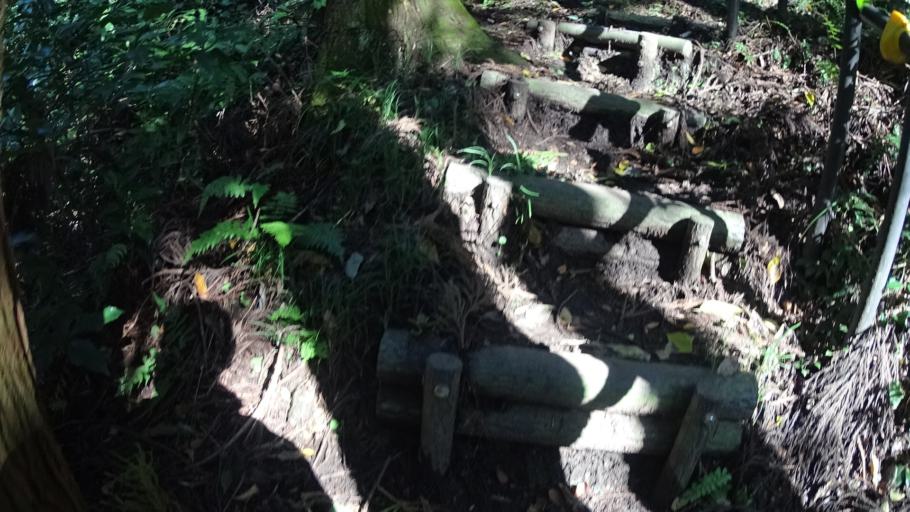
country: JP
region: Kanagawa
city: Zushi
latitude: 35.3572
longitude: 139.5993
